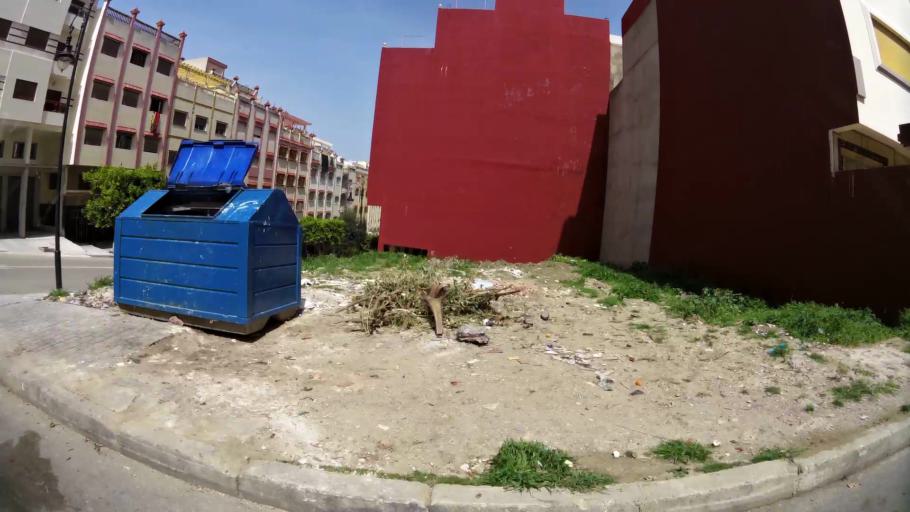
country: MA
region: Tanger-Tetouan
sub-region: Tanger-Assilah
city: Tangier
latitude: 35.7584
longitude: -5.8358
